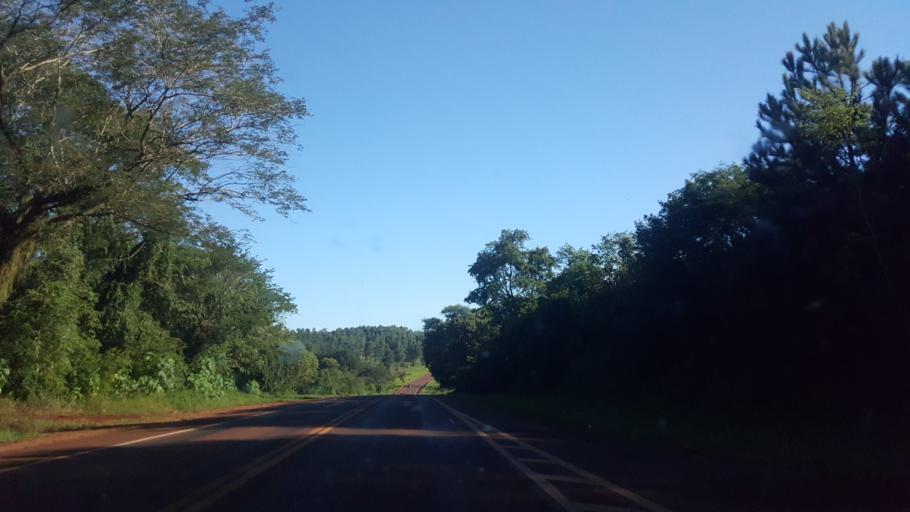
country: AR
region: Misiones
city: Puerto Esperanza
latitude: -26.1611
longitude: -54.5836
